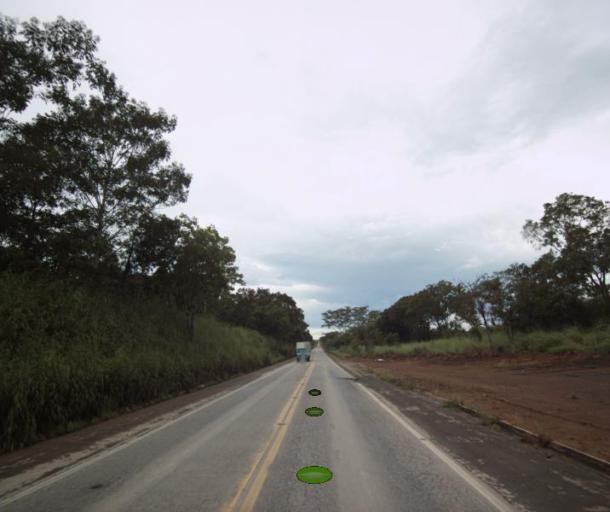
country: BR
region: Goias
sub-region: Porangatu
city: Porangatu
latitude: -13.5527
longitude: -49.0880
